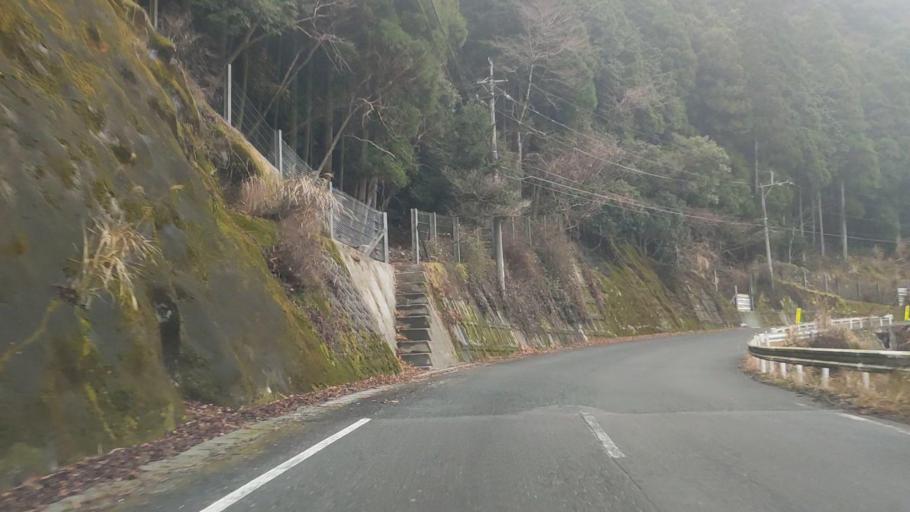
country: JP
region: Kumamoto
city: Matsubase
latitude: 32.6044
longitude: 130.8866
